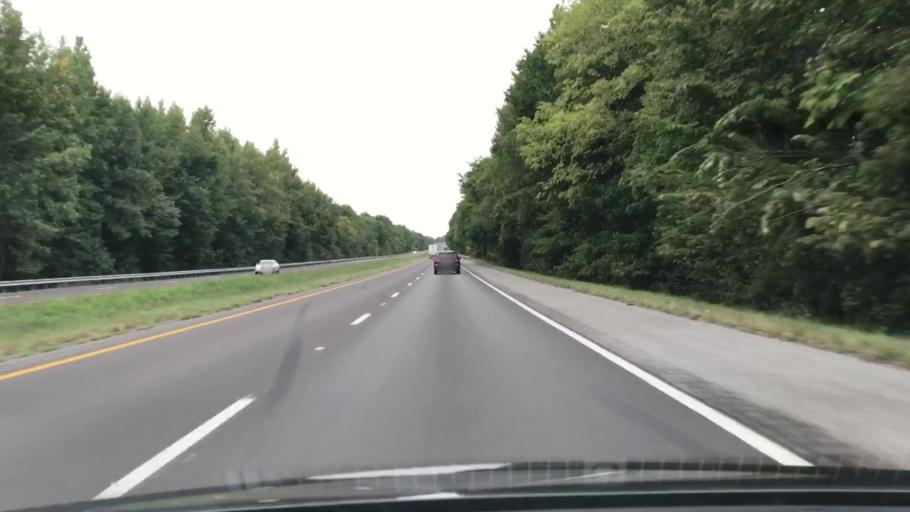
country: US
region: Kentucky
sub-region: Fulton County
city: Fulton
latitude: 36.6007
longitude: -88.8006
